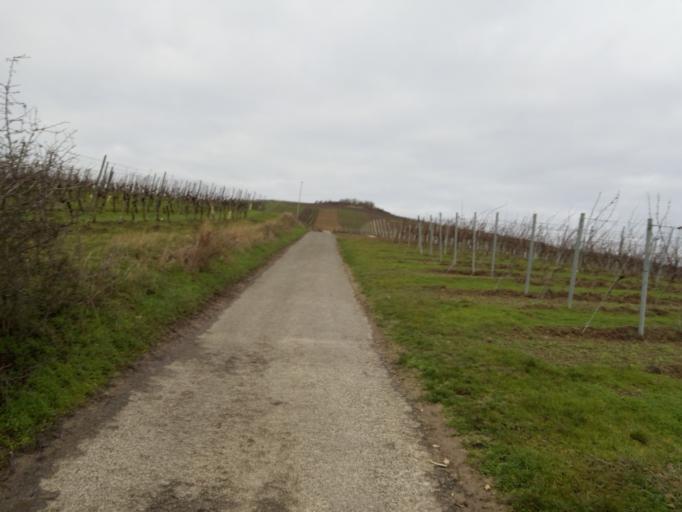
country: DE
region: Rheinland-Pfalz
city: Gau-Odernheim
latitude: 49.7905
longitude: 8.2072
